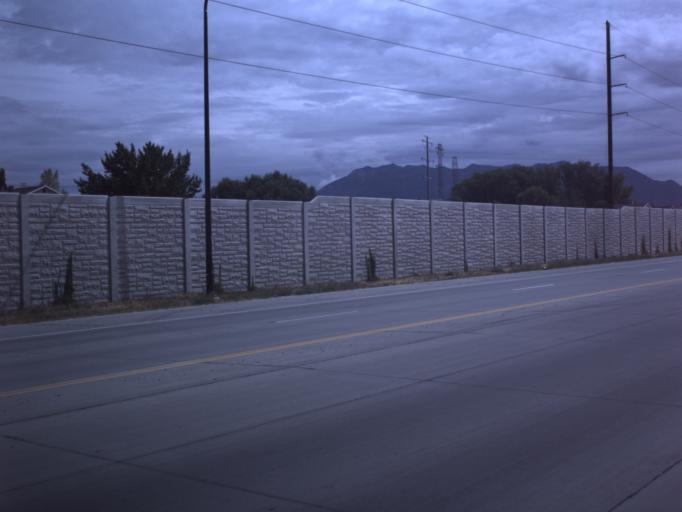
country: US
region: Utah
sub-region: Davis County
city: Syracuse
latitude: 41.1105
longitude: -112.0578
